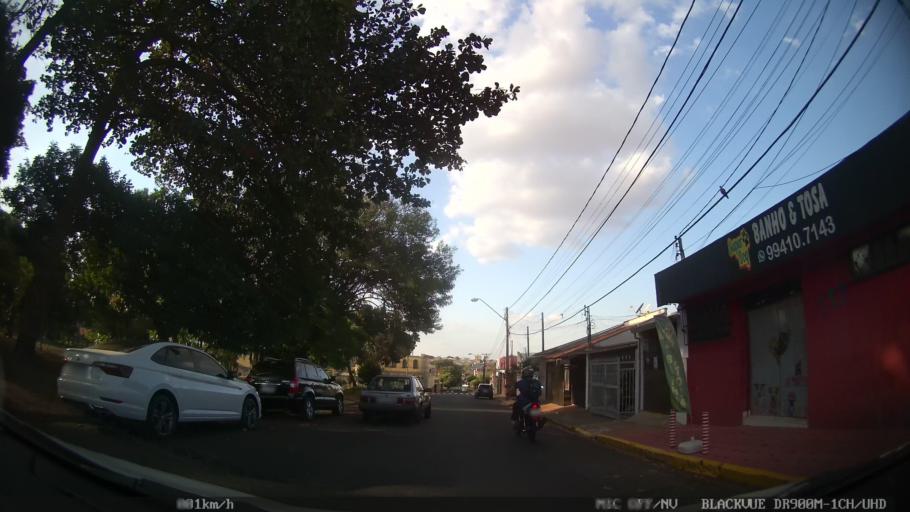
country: BR
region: Sao Paulo
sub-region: Ribeirao Preto
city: Ribeirao Preto
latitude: -21.1698
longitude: -47.8323
